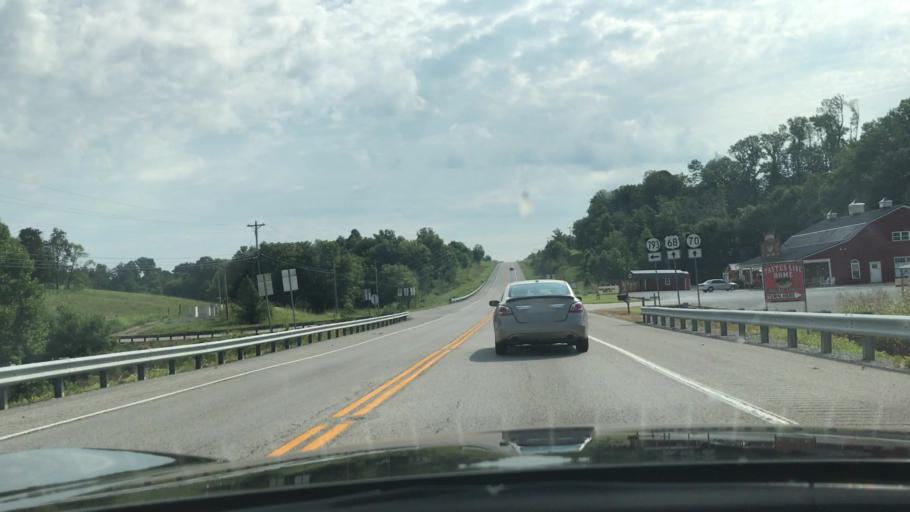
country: US
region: Kentucky
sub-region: Green County
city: Greensburg
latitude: 37.2941
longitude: -85.4674
